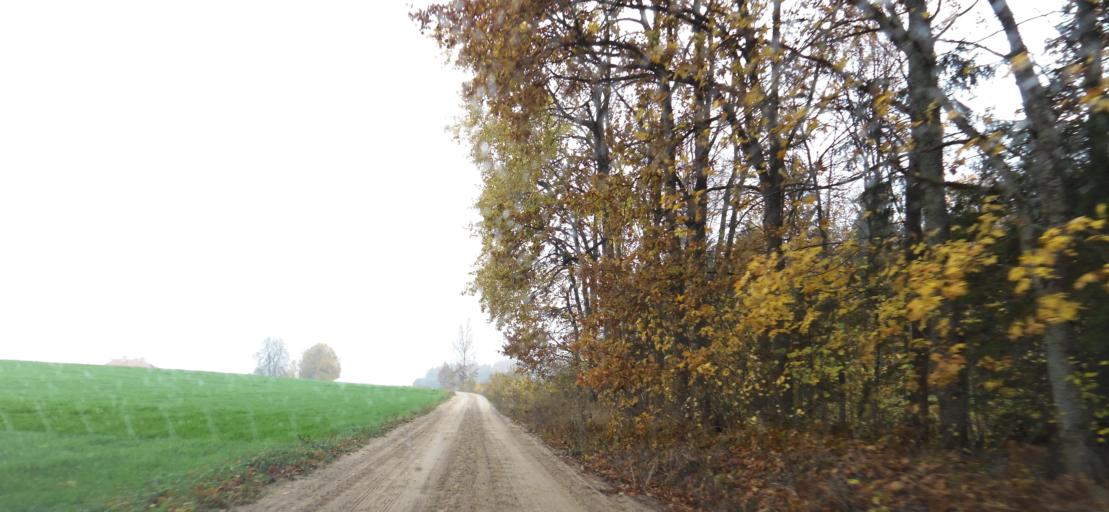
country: LT
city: Skaidiskes
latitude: 54.6239
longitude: 25.4735
